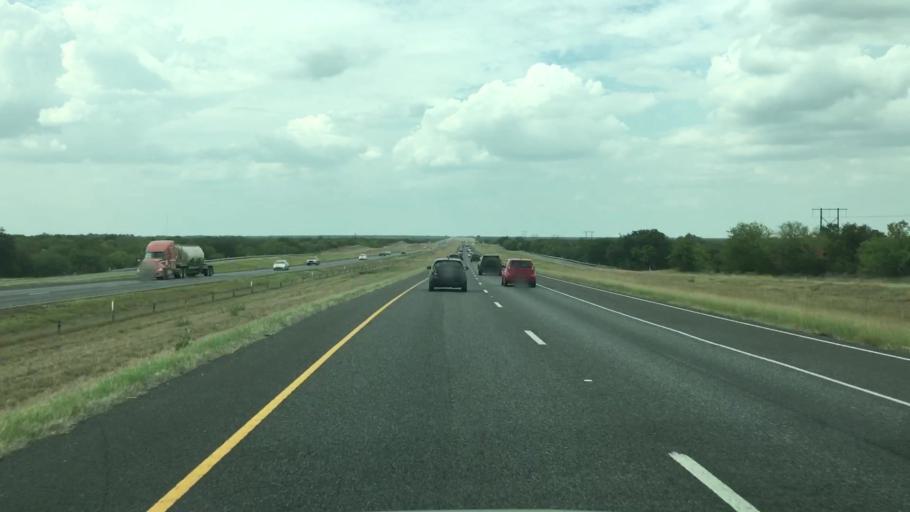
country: US
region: Texas
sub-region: Atascosa County
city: Pleasanton
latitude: 28.8297
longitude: -98.3680
